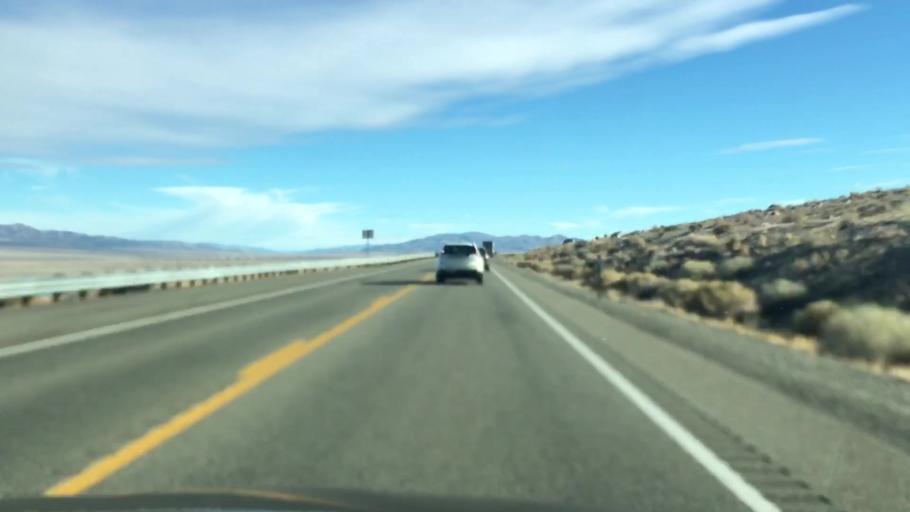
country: US
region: Nevada
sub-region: Mineral County
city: Hawthorne
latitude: 38.6136
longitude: -118.7229
